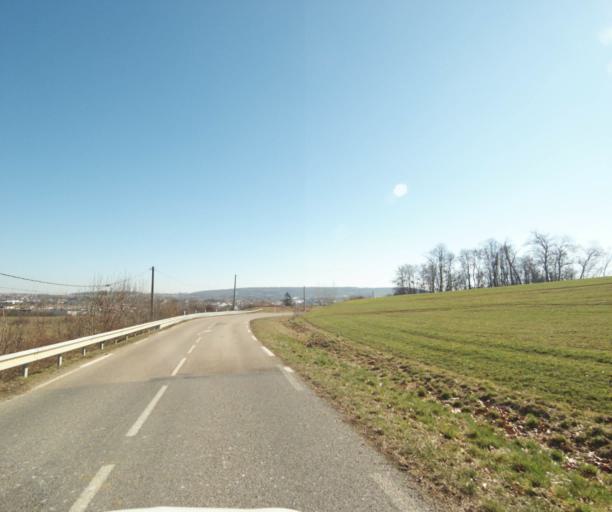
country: FR
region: Lorraine
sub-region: Departement de Meurthe-et-Moselle
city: Essey-les-Nancy
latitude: 48.7148
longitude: 6.2399
